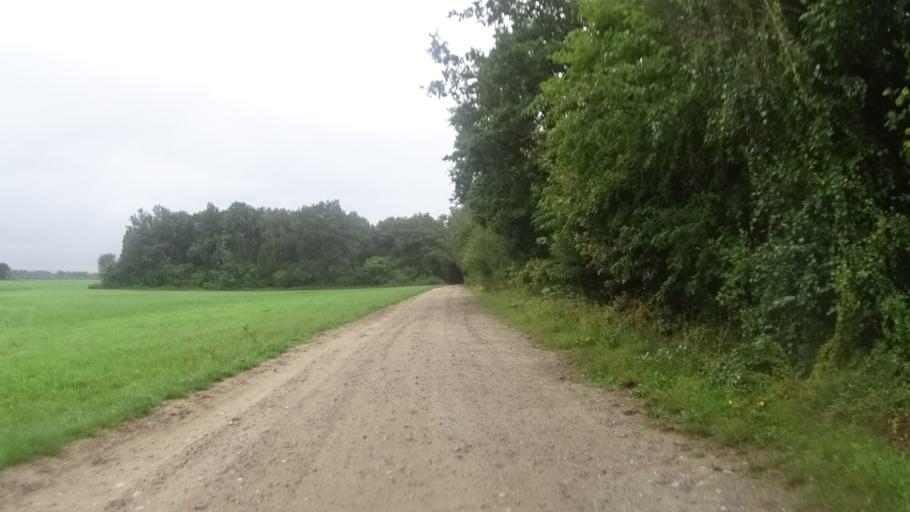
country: DE
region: Schleswig-Holstein
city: Dalldorf
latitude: 53.4158
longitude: 10.6109
